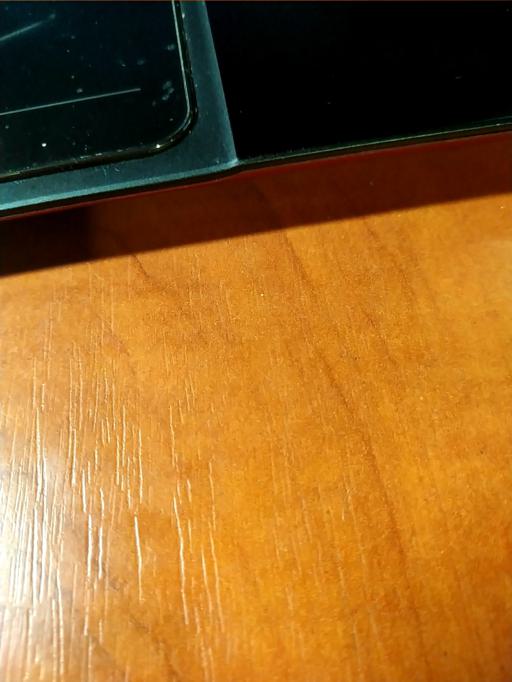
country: RU
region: Tverskaya
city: Zubtsov
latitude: 56.3269
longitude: 34.6753
